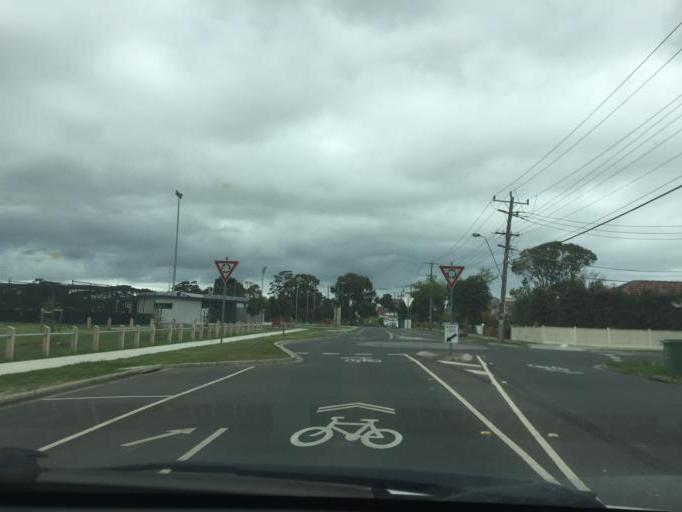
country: AU
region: Victoria
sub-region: Maribyrnong
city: Kingsville
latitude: -37.8165
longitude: 144.8686
